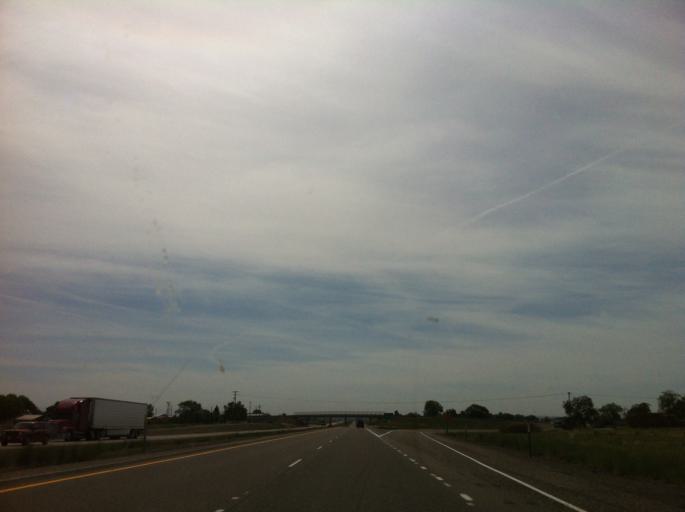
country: US
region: Oregon
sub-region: Malheur County
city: Ontario
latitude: 44.0871
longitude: -117.0223
